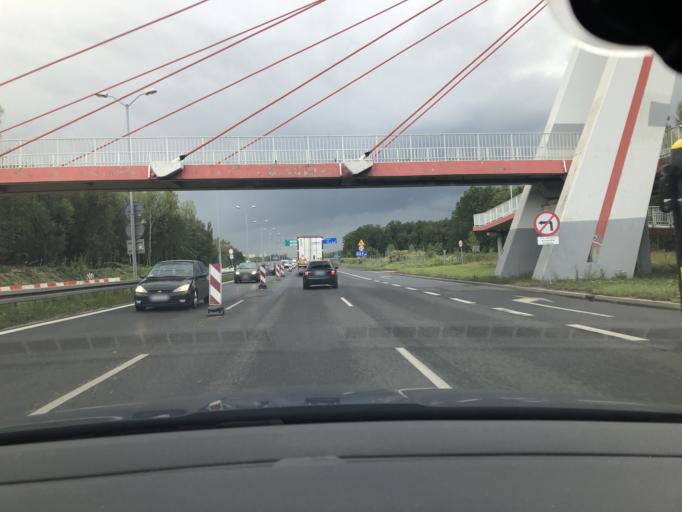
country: PL
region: Silesian Voivodeship
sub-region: Katowice
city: Katowice
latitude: 50.2354
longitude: 19.0545
